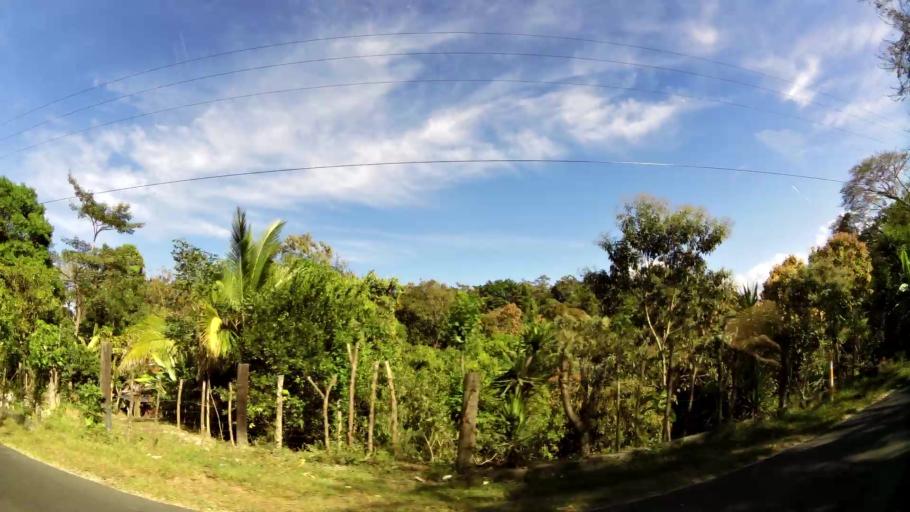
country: SV
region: Cuscatlan
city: Tenancingo
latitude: 13.8379
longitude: -89.0283
